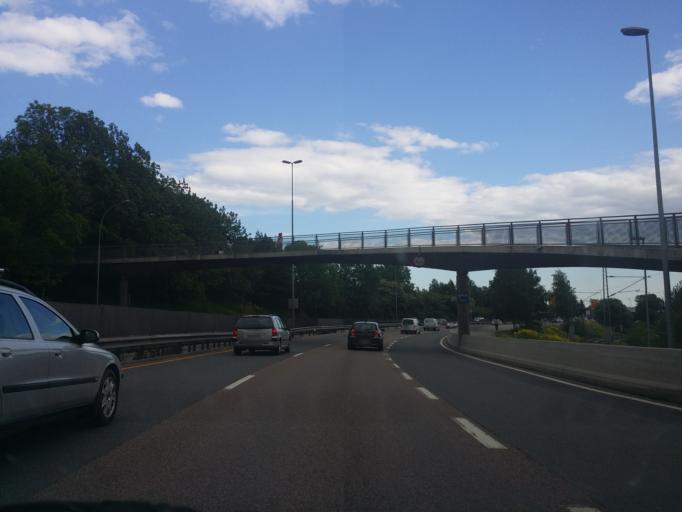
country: NO
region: Oslo
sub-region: Oslo
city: Oslo
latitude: 59.9510
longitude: 10.7761
